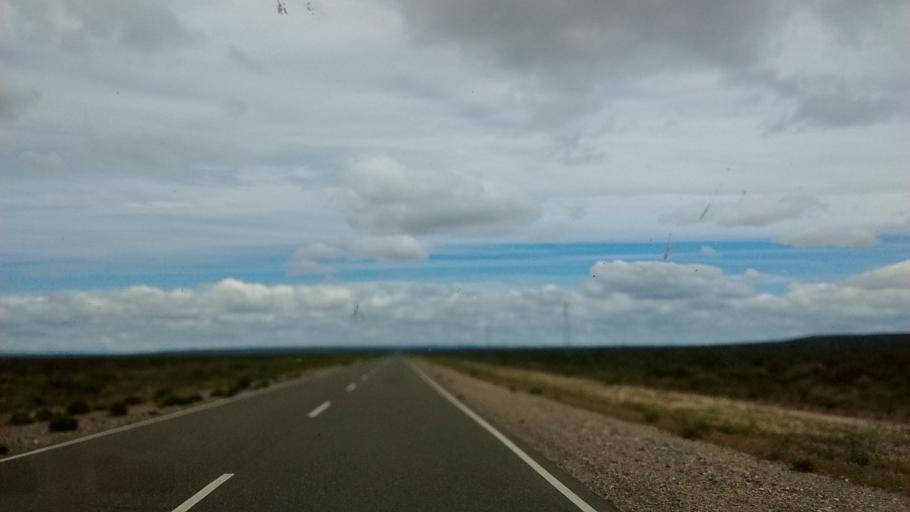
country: AR
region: Neuquen
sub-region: Departamento de Picun Leufu
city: Picun Leufu
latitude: -39.6771
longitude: -69.4544
